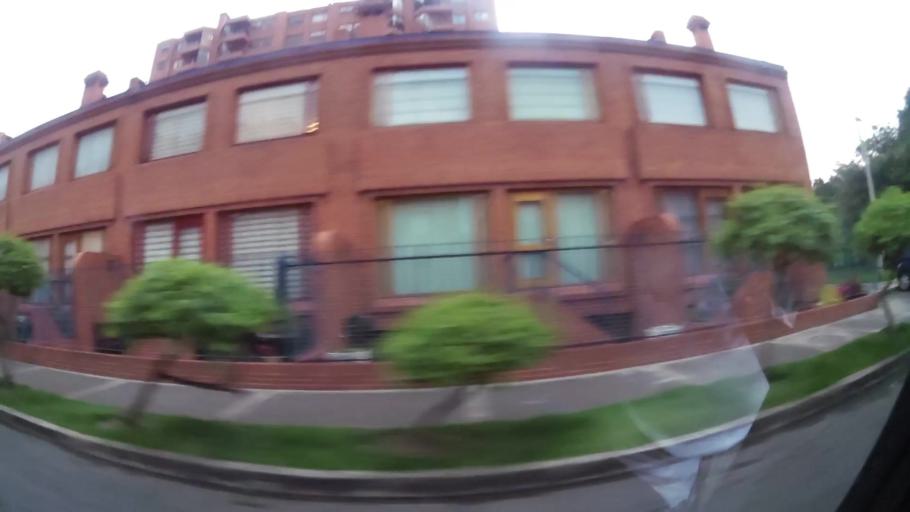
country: CO
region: Bogota D.C.
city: Barrio San Luis
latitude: 4.7247
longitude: -74.0635
